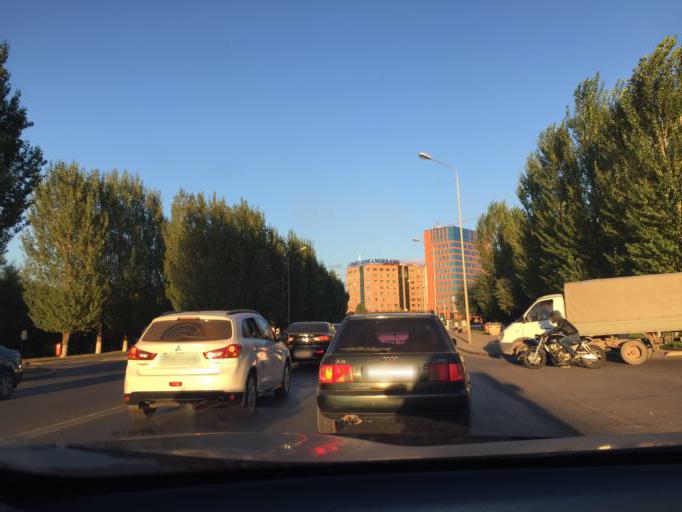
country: KZ
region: Astana Qalasy
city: Astana
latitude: 51.1468
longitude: 71.4191
